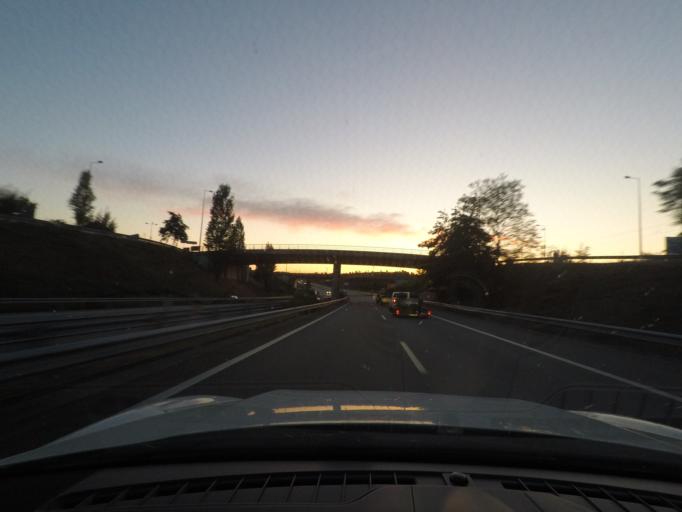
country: PT
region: Porto
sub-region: Pacos de Ferreira
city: Frazao
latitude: 41.2572
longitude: -8.3976
